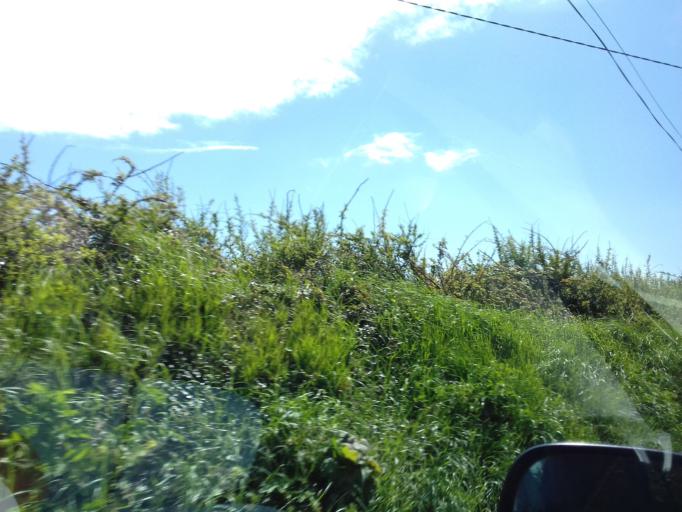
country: IE
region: Munster
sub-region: Waterford
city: Dunmore East
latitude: 52.2173
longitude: -6.8596
